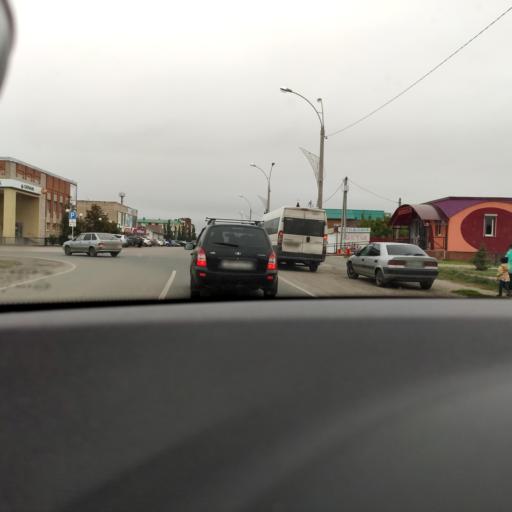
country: RU
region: Samara
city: Krasnyy Yar
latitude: 53.4954
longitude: 50.3887
